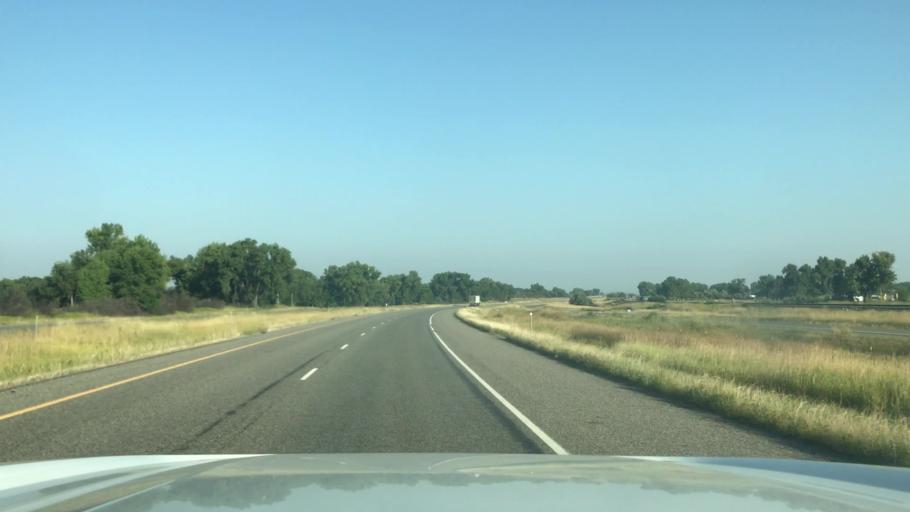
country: US
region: Montana
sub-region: Big Horn County
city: Hardin
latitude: 45.7182
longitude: -107.5415
